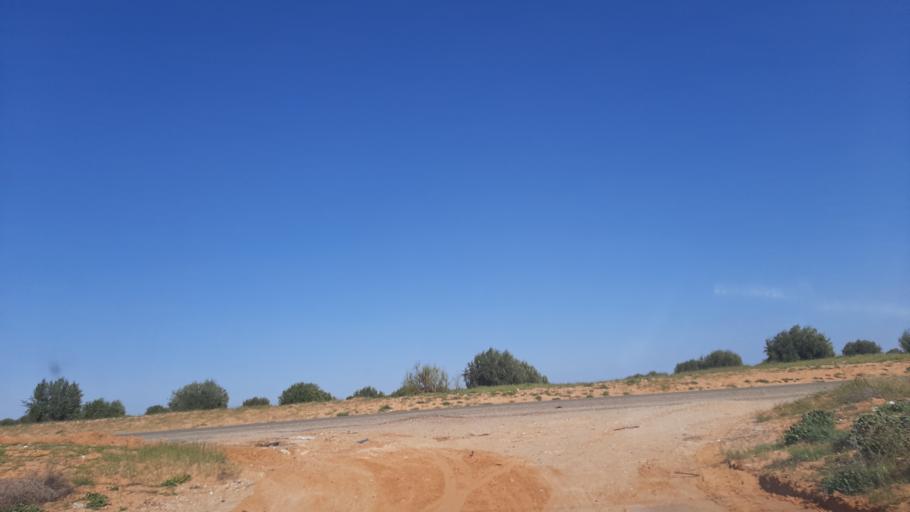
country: TN
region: Madanin
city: Medenine
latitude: 33.2859
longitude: 10.7873
